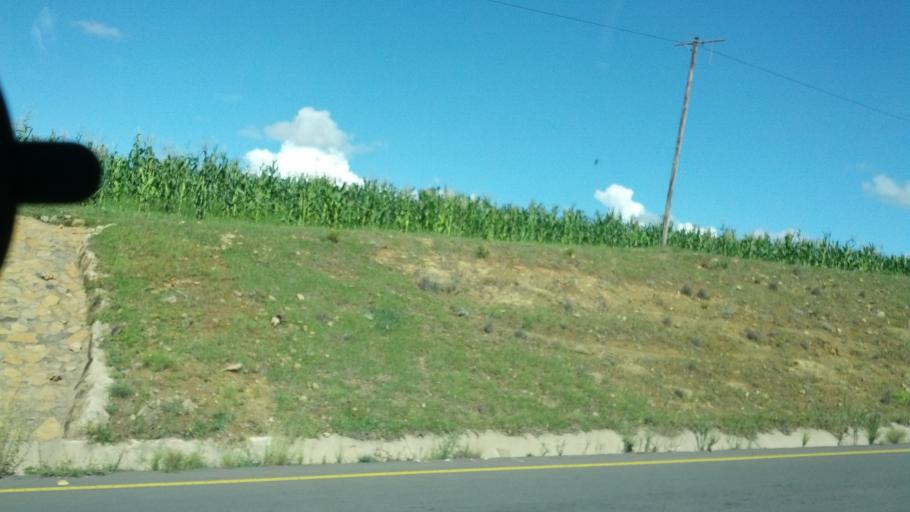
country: LS
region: Maseru
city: Maseru
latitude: -29.5381
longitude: 27.5097
